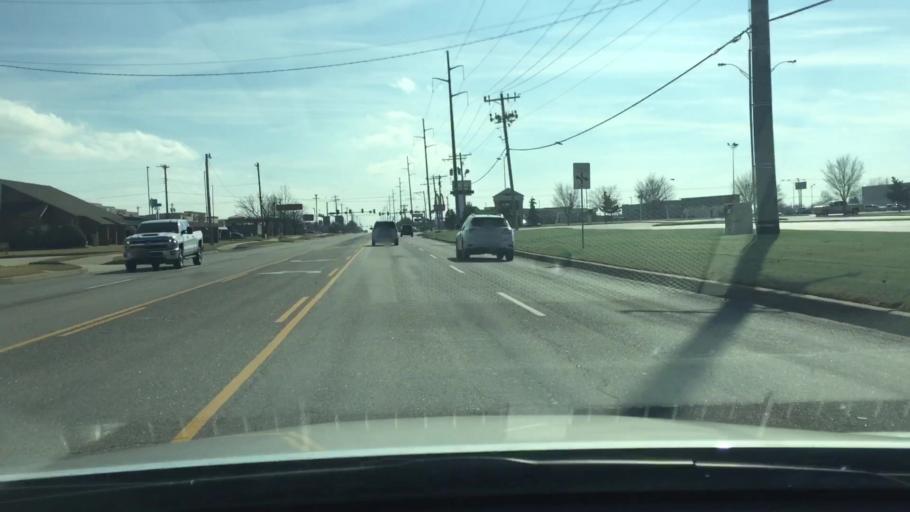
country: US
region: Oklahoma
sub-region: Cleveland County
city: Moore
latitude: 35.3798
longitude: -97.5479
